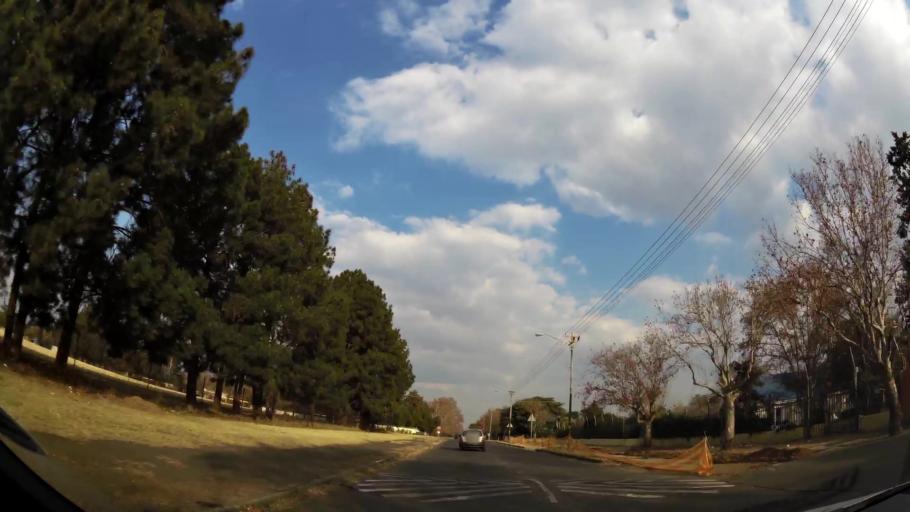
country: ZA
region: Gauteng
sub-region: Ekurhuleni Metropolitan Municipality
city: Germiston
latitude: -26.2432
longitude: 28.1713
